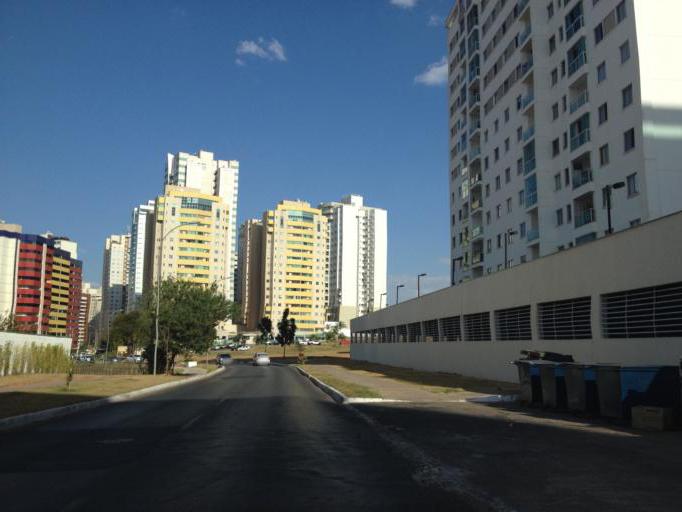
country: BR
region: Federal District
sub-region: Brasilia
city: Brasilia
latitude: -15.8338
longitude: -48.0348
